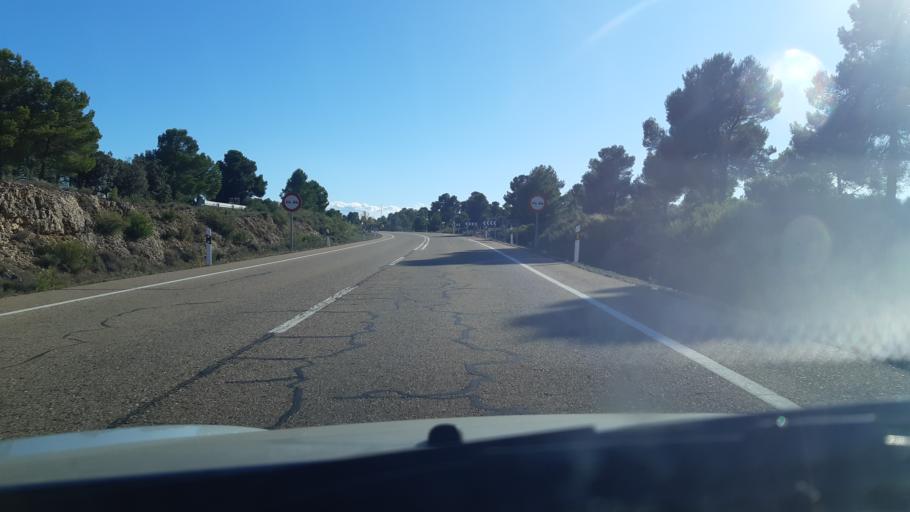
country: ES
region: Aragon
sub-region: Provincia de Teruel
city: Fornoles
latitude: 40.9342
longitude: -0.0122
